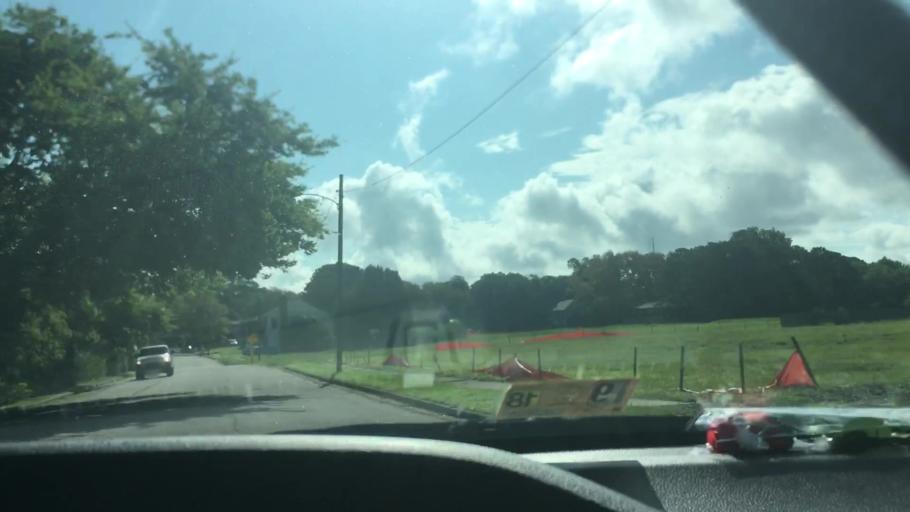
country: US
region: Virginia
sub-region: City of Portsmouth
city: Portsmouth Heights
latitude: 36.8480
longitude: -76.3420
